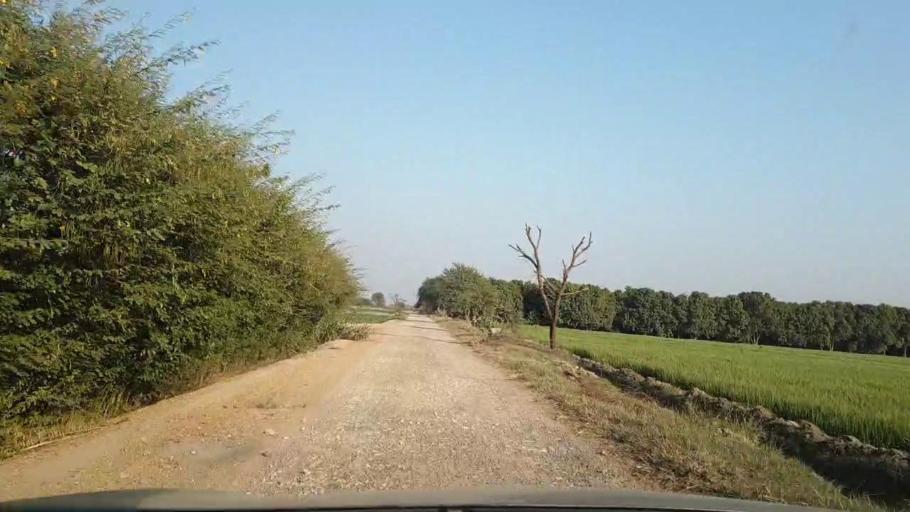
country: PK
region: Sindh
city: Tando Allahyar
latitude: 25.5732
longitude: 68.7767
